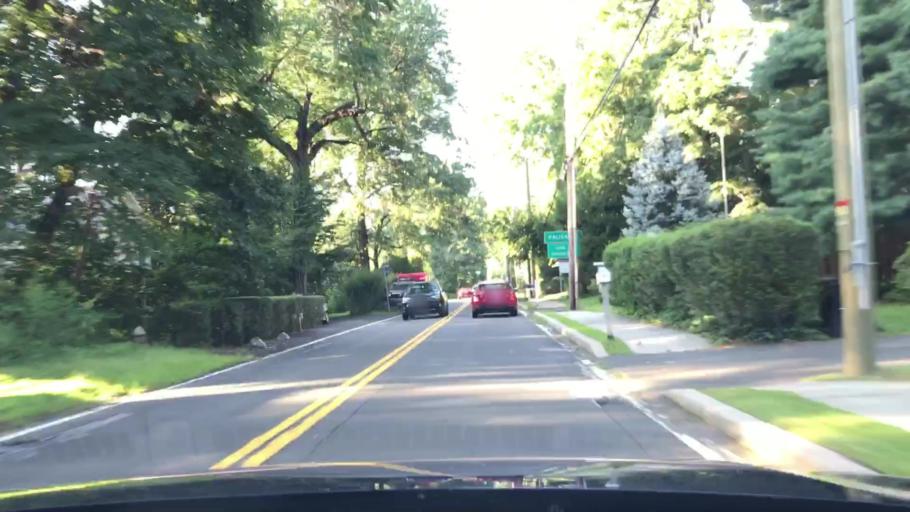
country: US
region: New York
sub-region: Rockland County
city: Sparkill
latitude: 41.0129
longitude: -73.9292
